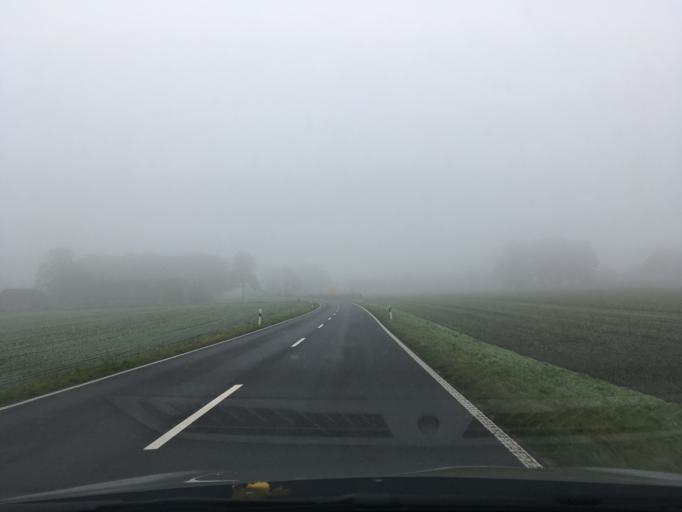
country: DE
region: North Rhine-Westphalia
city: Stadtlohn
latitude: 52.0602
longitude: 6.9376
